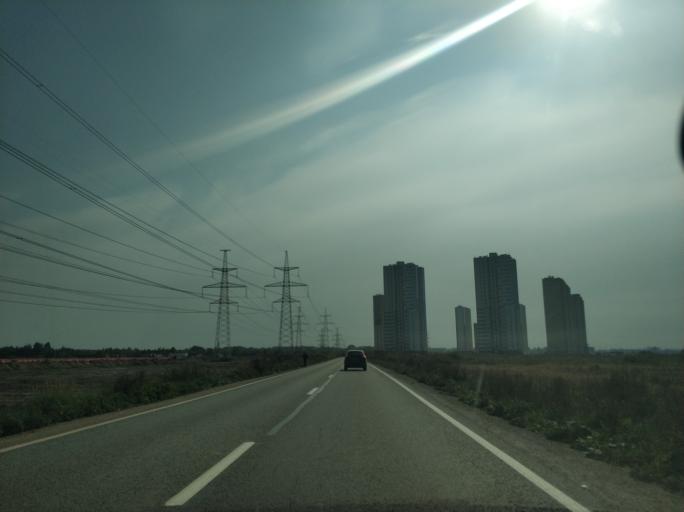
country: RU
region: Leningrad
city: Murino
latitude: 60.0148
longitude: 30.4751
